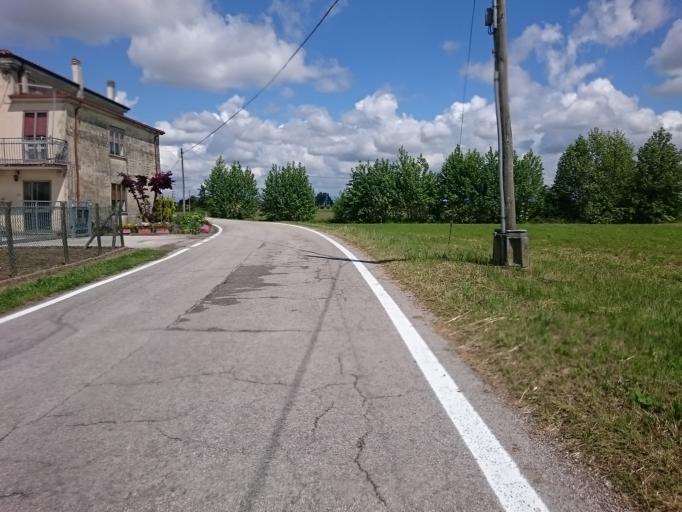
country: IT
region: Veneto
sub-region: Provincia di Padova
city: Campodoro
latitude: 45.4776
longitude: 11.7390
